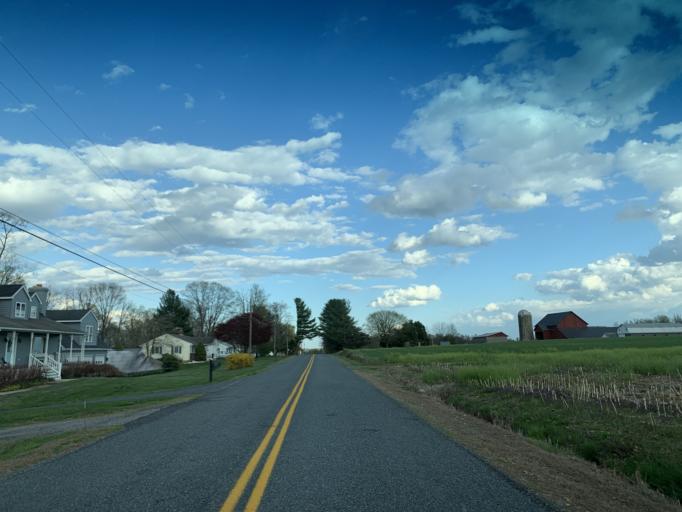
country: US
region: Maryland
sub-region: Harford County
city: South Bel Air
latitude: 39.5976
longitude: -76.3160
